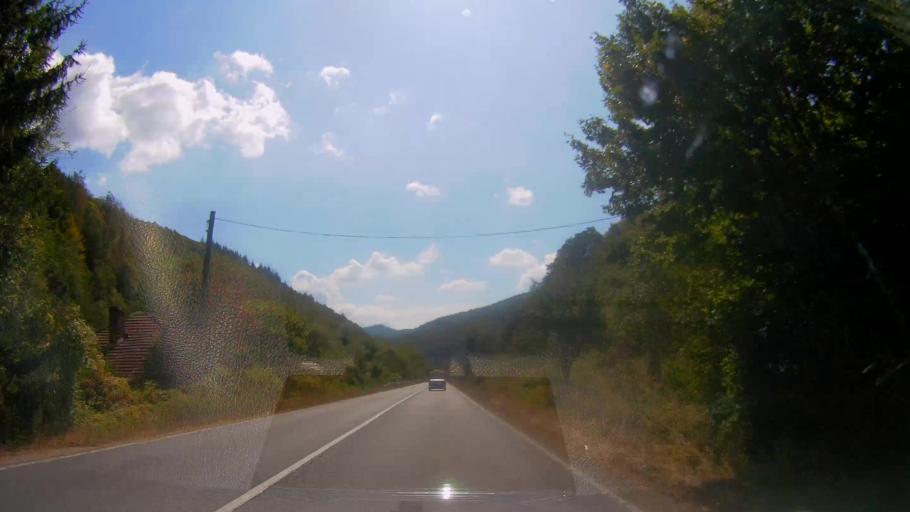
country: BG
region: Stara Zagora
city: Gurkovo
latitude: 42.7445
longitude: 25.7093
